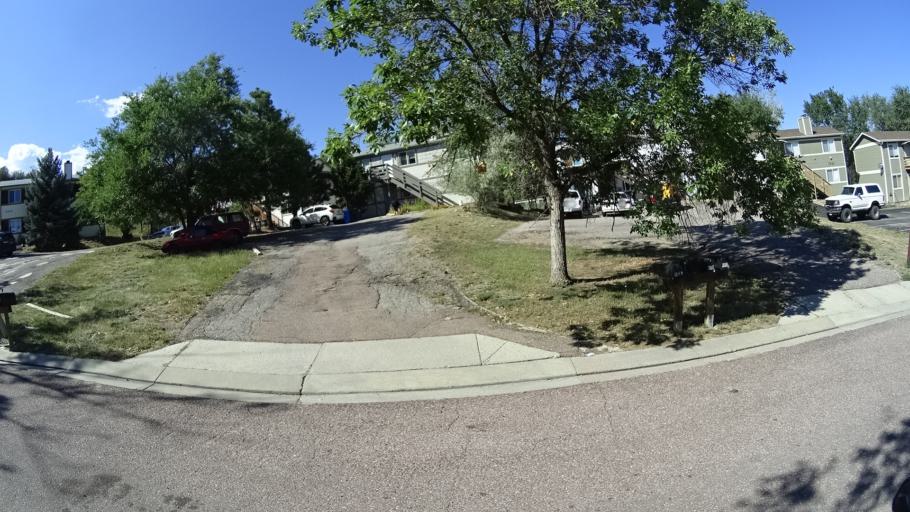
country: US
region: Colorado
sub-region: El Paso County
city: Colorado Springs
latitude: 38.8532
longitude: -104.8516
